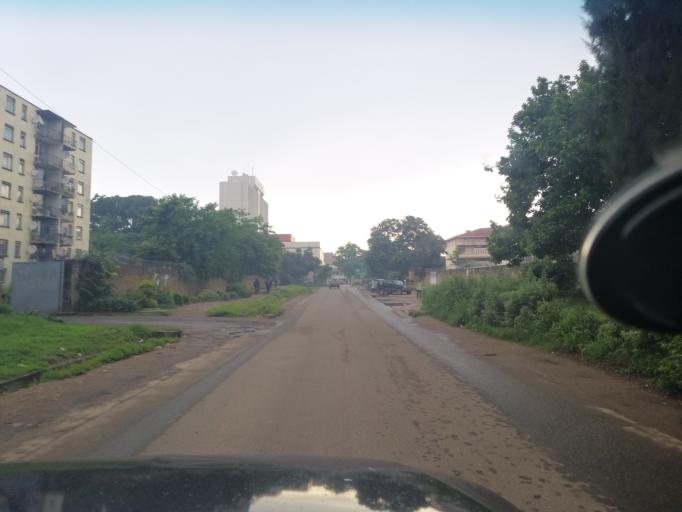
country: ZM
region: Lusaka
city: Lusaka
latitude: -15.4215
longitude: 28.2933
